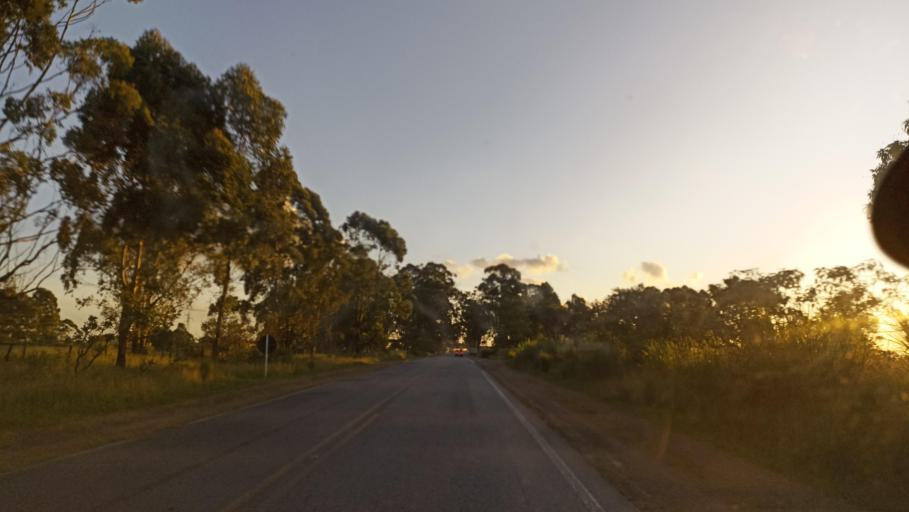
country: BR
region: Minas Gerais
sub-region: Sao Joao Del Rei
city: Sao Joao del Rei
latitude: -21.2396
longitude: -44.3996
